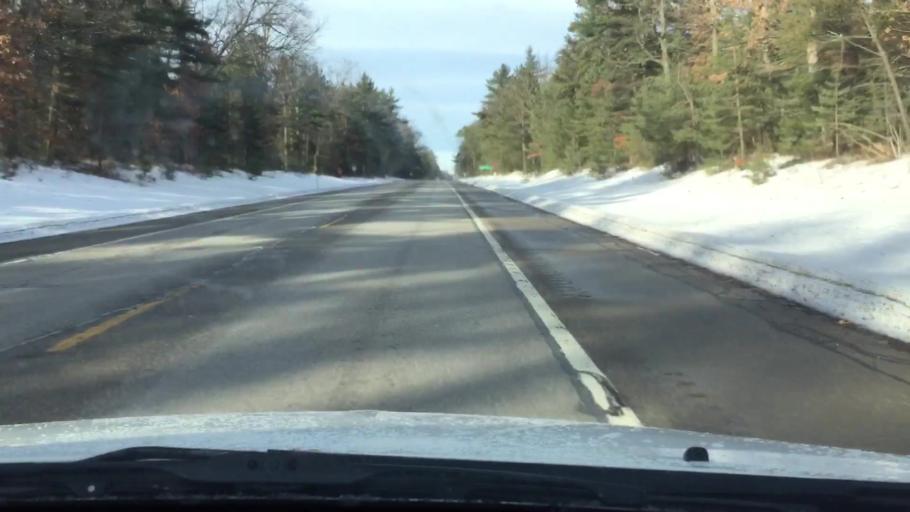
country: US
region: Michigan
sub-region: Wexford County
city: Manton
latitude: 44.5522
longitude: -85.3692
